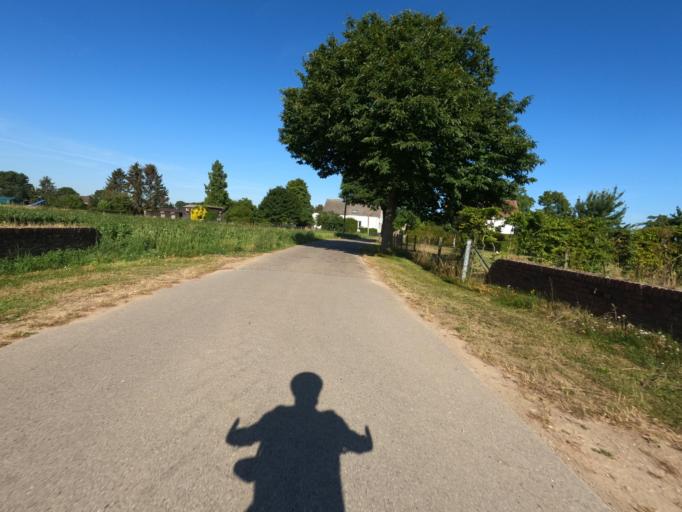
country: DE
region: North Rhine-Westphalia
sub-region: Regierungsbezirk Koln
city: Heinsberg
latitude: 51.0809
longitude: 6.1175
